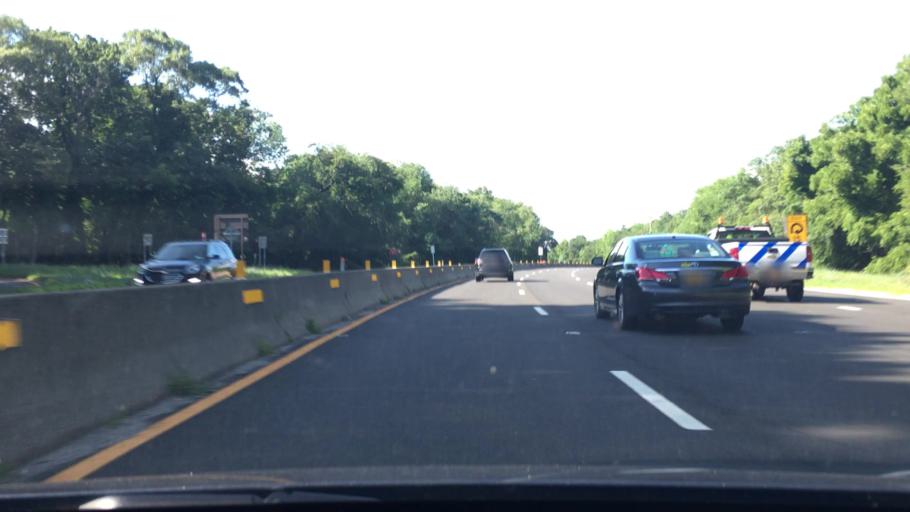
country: US
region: New York
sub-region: Nassau County
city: Bellmore
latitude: 40.6709
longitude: -73.5145
